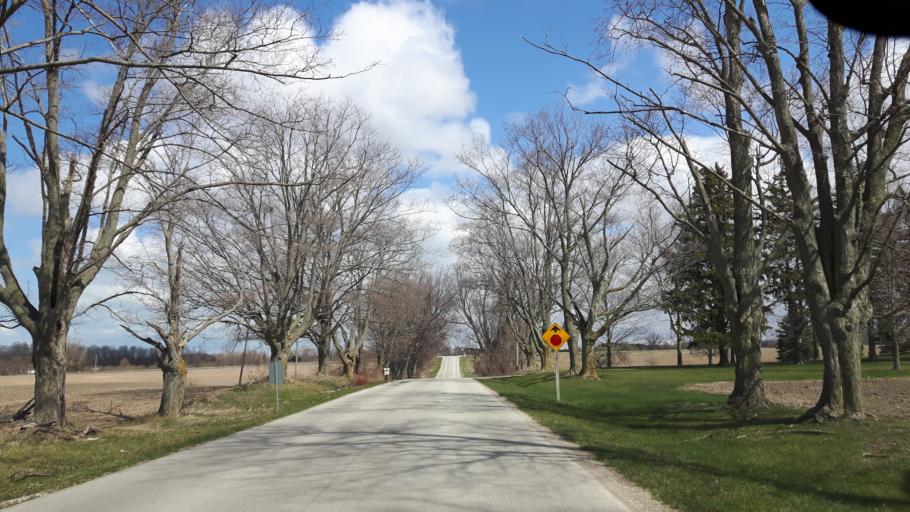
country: CA
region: Ontario
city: Goderich
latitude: 43.6395
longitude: -81.6846
